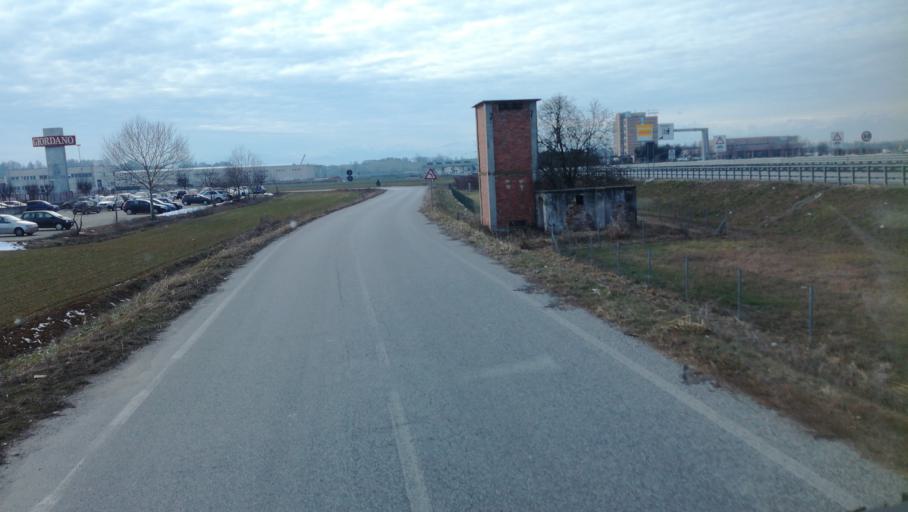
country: IT
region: Piedmont
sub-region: Provincia di Cuneo
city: Cervere
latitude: 44.6630
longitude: 7.7849
